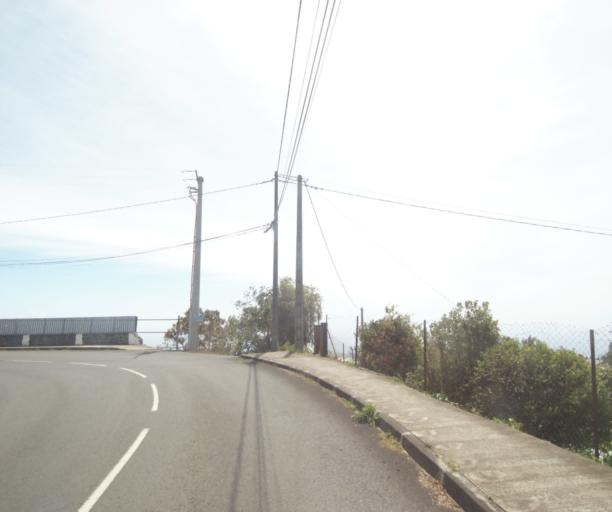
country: RE
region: Reunion
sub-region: Reunion
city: Trois-Bassins
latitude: -21.0593
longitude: 55.3082
